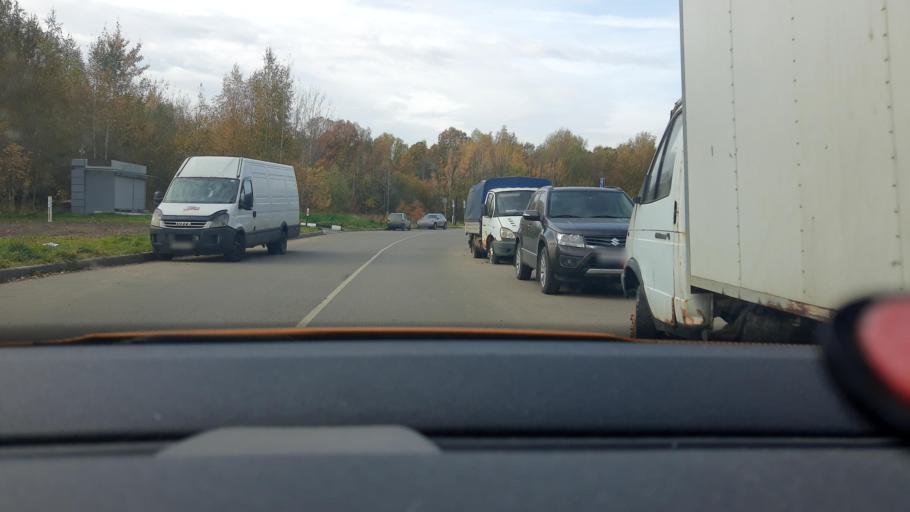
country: RU
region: Moskovskaya
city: Krasnogorsk
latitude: 55.8277
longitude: 37.2961
